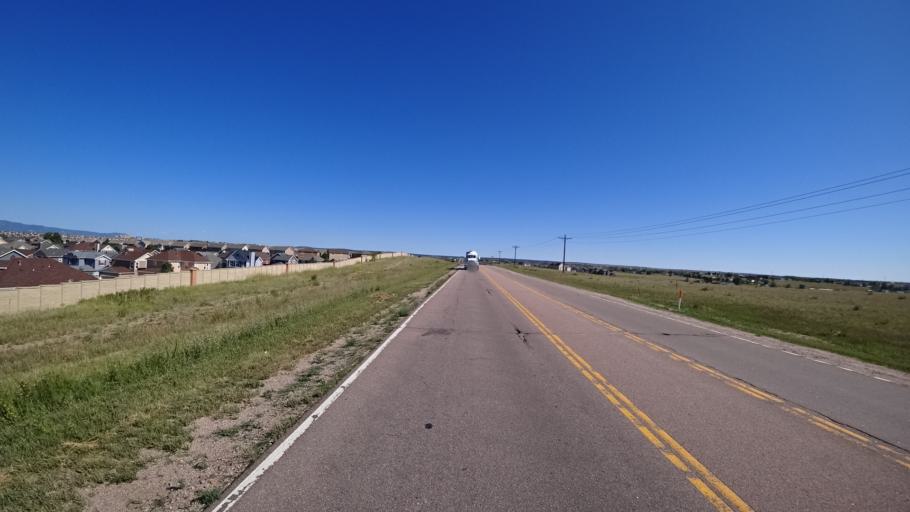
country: US
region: Colorado
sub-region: El Paso County
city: Cimarron Hills
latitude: 38.9143
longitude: -104.6829
